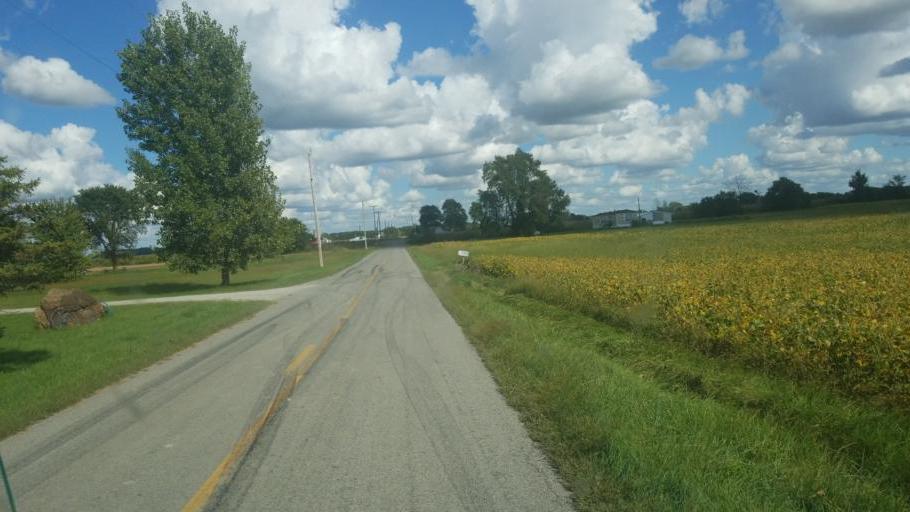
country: US
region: Ohio
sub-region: Hardin County
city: Kenton
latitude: 40.5071
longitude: -83.5644
